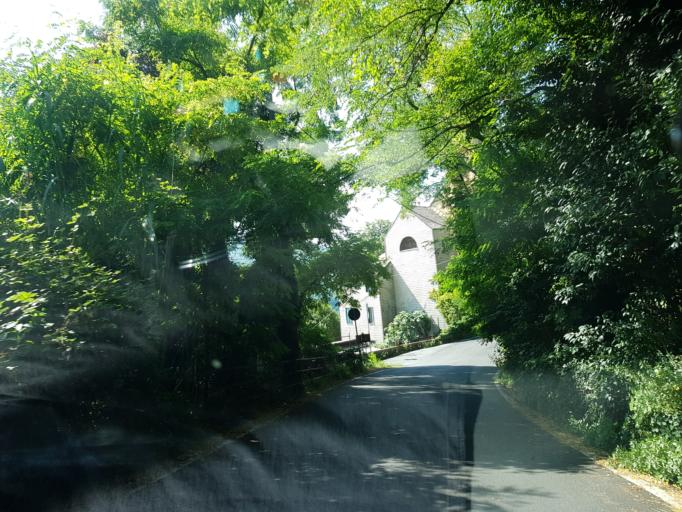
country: IT
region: Liguria
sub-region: Provincia di Genova
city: Manesseno
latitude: 44.4781
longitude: 8.9095
